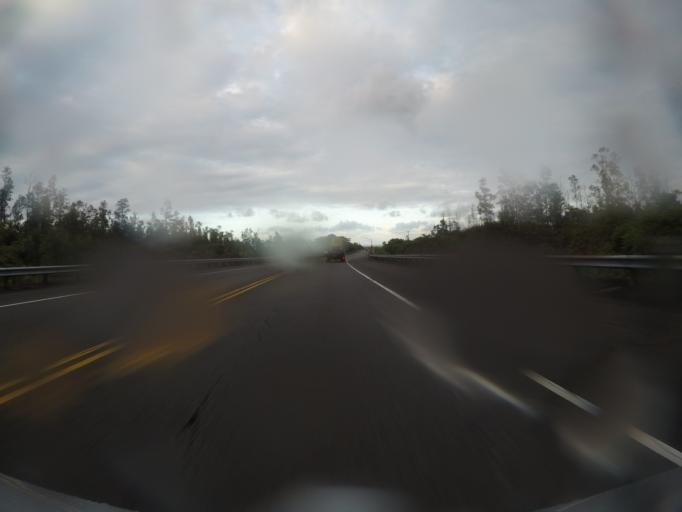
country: US
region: Hawaii
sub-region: Hawaii County
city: Hilo
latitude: 19.6923
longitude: -155.1121
